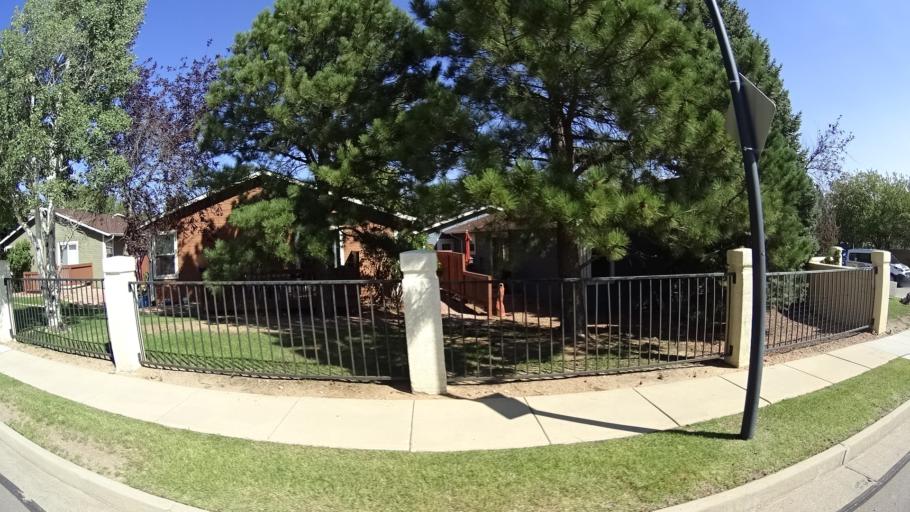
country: US
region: Colorado
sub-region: El Paso County
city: Colorado Springs
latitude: 38.8304
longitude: -104.8720
